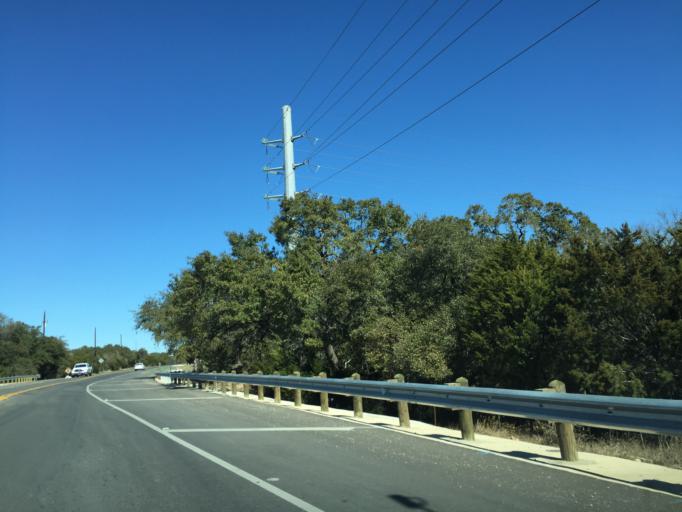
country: US
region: Texas
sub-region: Bexar County
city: Timberwood Park
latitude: 29.6872
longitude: -98.4424
